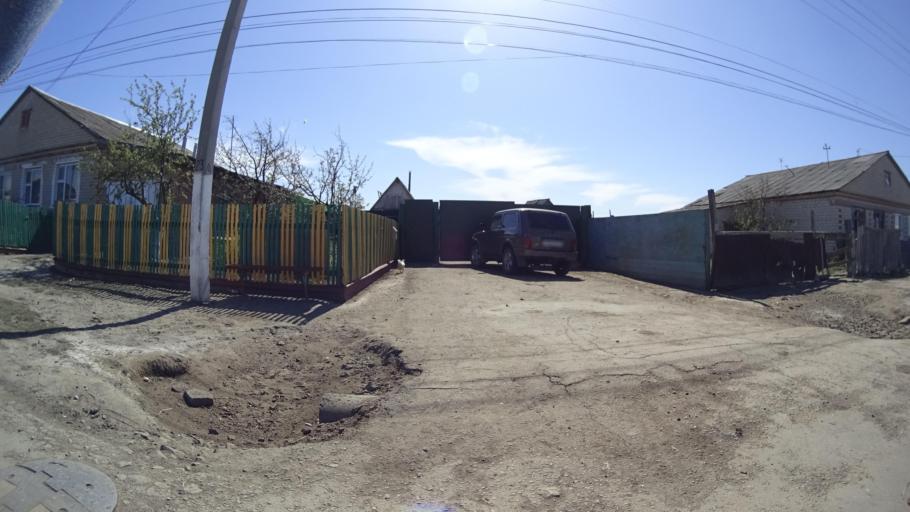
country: RU
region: Chelyabinsk
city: Chesma
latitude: 53.7953
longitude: 61.0333
